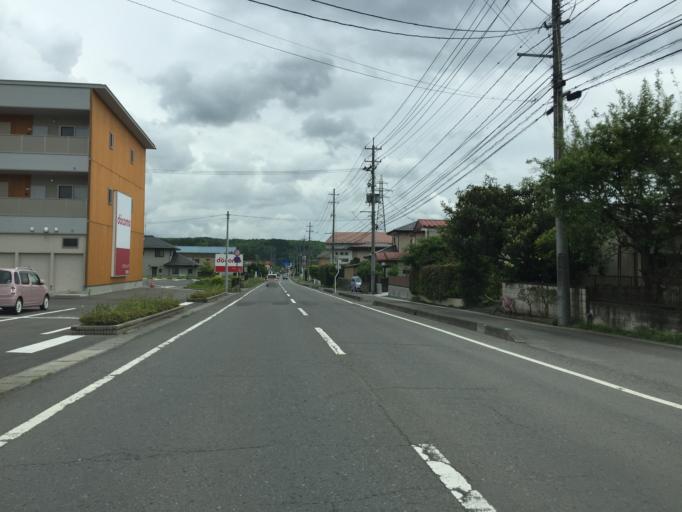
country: JP
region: Fukushima
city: Ishikawa
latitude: 37.0351
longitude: 140.3876
